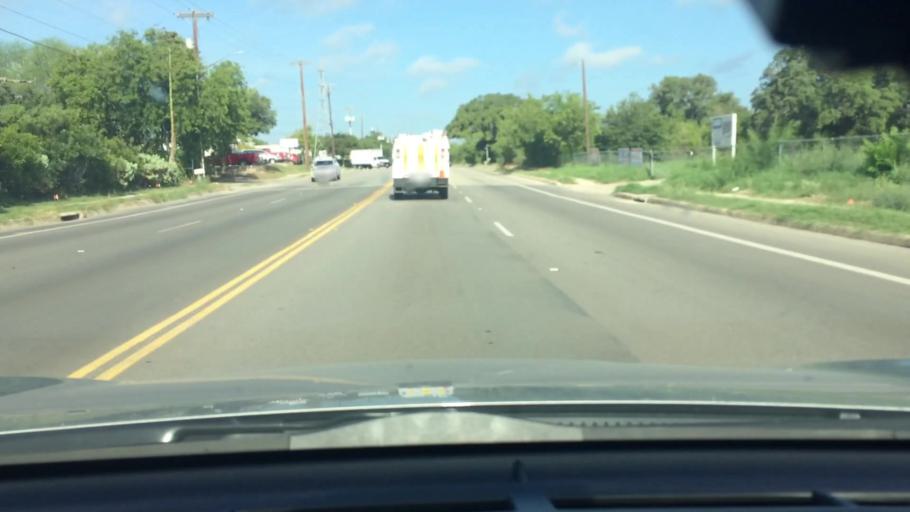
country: US
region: Texas
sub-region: Bexar County
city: China Grove
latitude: 29.3742
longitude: -98.4001
